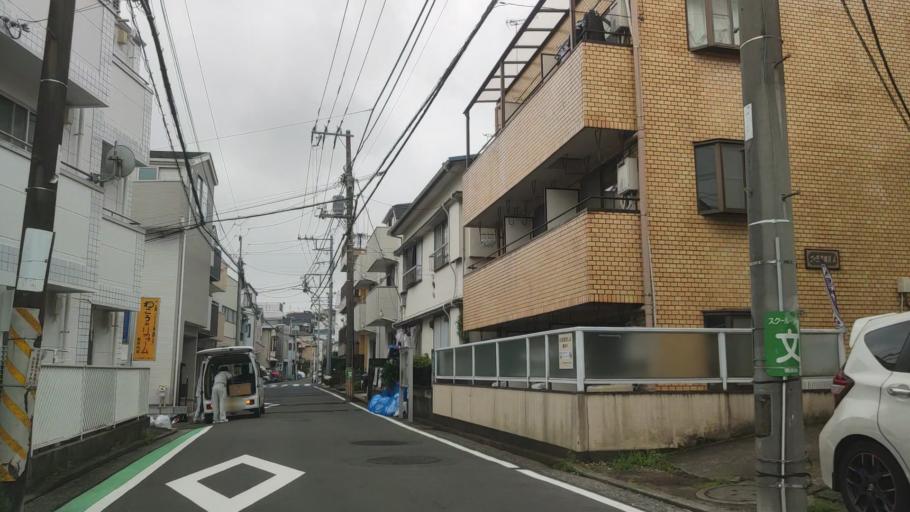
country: JP
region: Kanagawa
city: Yokohama
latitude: 35.4465
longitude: 139.6061
